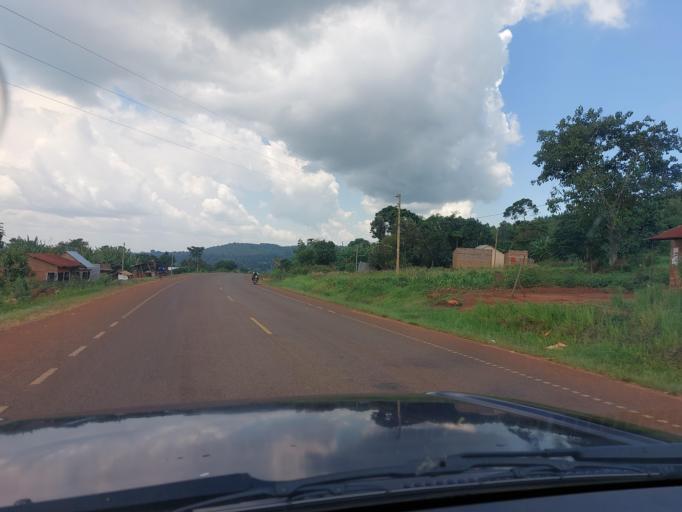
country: UG
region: Central Region
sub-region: Buikwe District
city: Njeru
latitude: 0.3338
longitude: 33.1212
